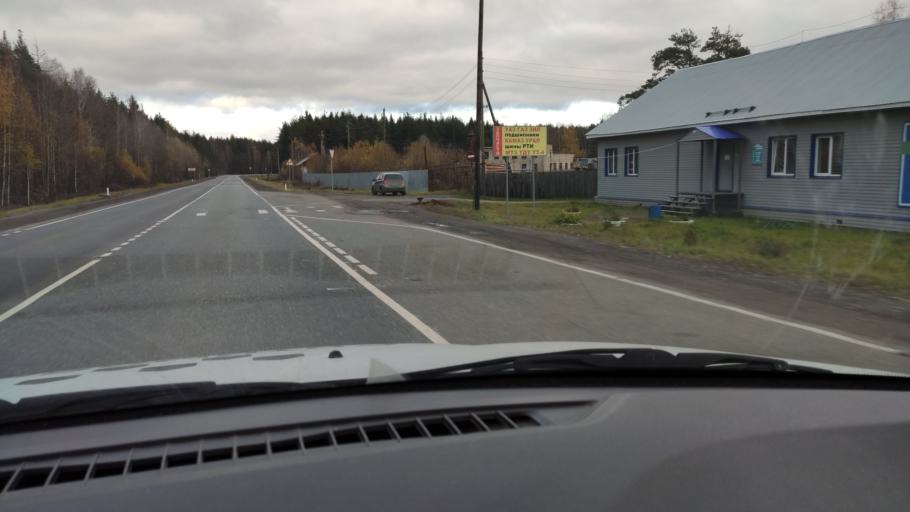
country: RU
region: Kirov
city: Belaya Kholunitsa
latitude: 58.8706
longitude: 50.8450
